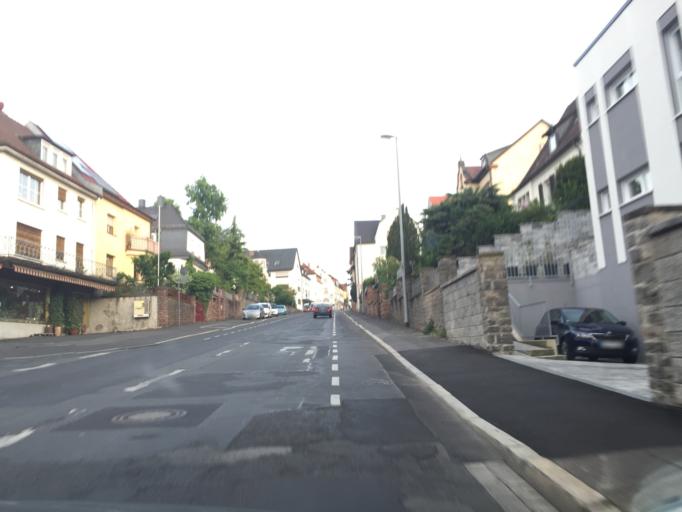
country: DE
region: Bavaria
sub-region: Regierungsbezirk Unterfranken
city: Aschaffenburg
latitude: 49.9642
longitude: 9.1588
